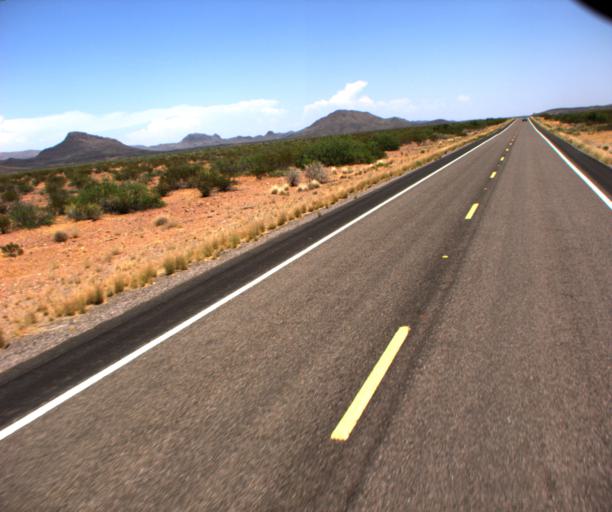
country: US
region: Arizona
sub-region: Graham County
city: Swift Trail Junction
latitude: 32.7622
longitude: -109.4451
